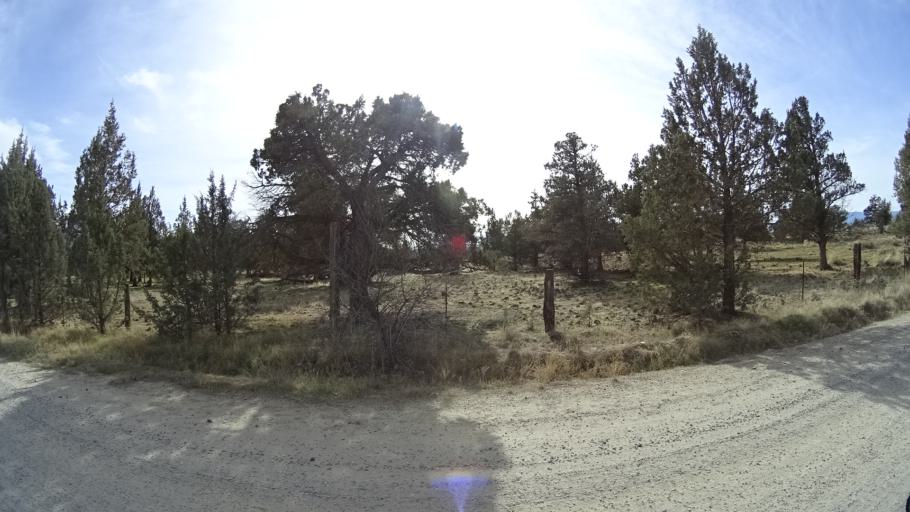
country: US
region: California
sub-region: Siskiyou County
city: Montague
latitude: 41.5953
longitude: -122.4156
